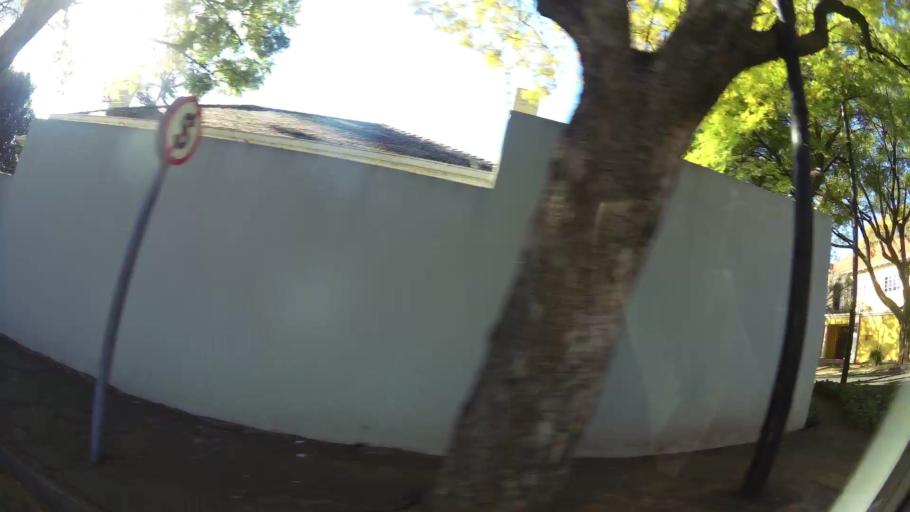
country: ZA
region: Gauteng
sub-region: City of Johannesburg Metropolitan Municipality
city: Johannesburg
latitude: -26.1935
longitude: 28.0880
